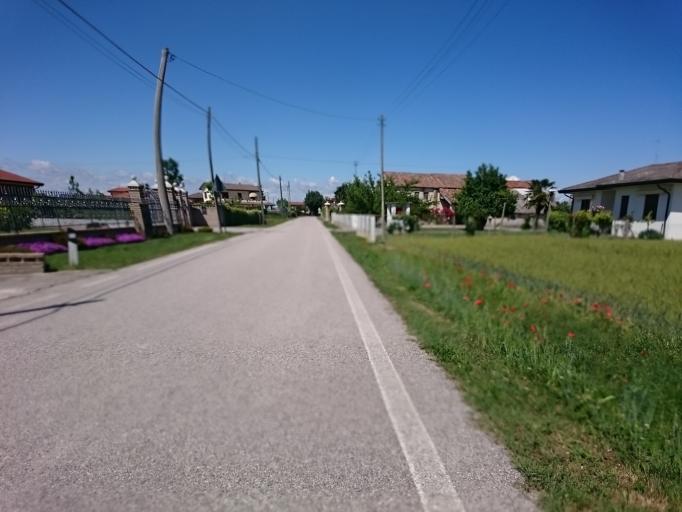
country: IT
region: Veneto
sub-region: Provincia di Padova
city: Codevigo
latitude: 45.2514
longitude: 12.0993
